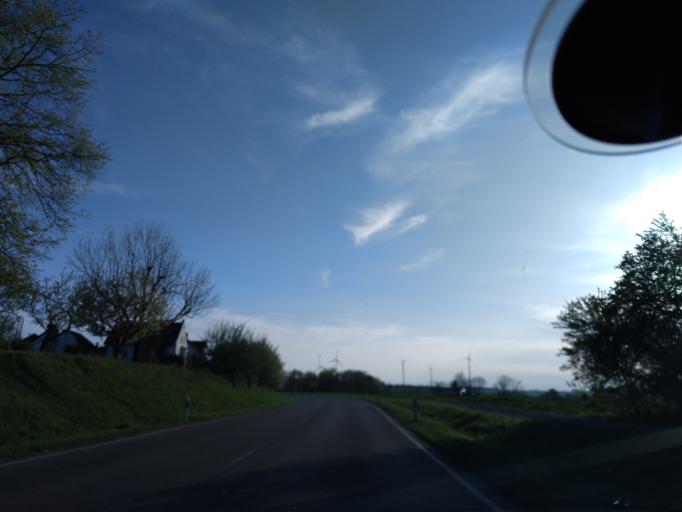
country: DE
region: Baden-Wuerttemberg
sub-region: Regierungsbezirk Stuttgart
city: Kirchberg an der Jagst
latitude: 49.1971
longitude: 9.9778
